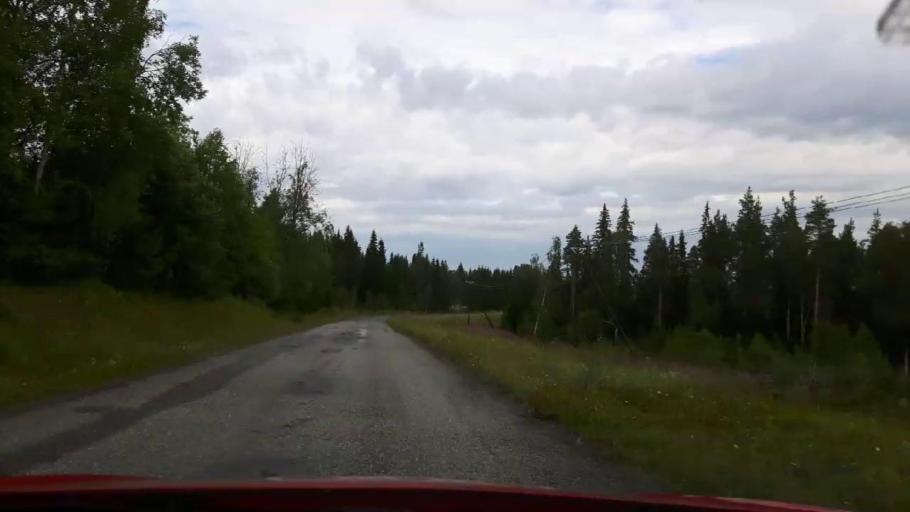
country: SE
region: Jaemtland
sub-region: Stroemsunds Kommun
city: Stroemsund
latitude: 63.5313
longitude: 15.3554
